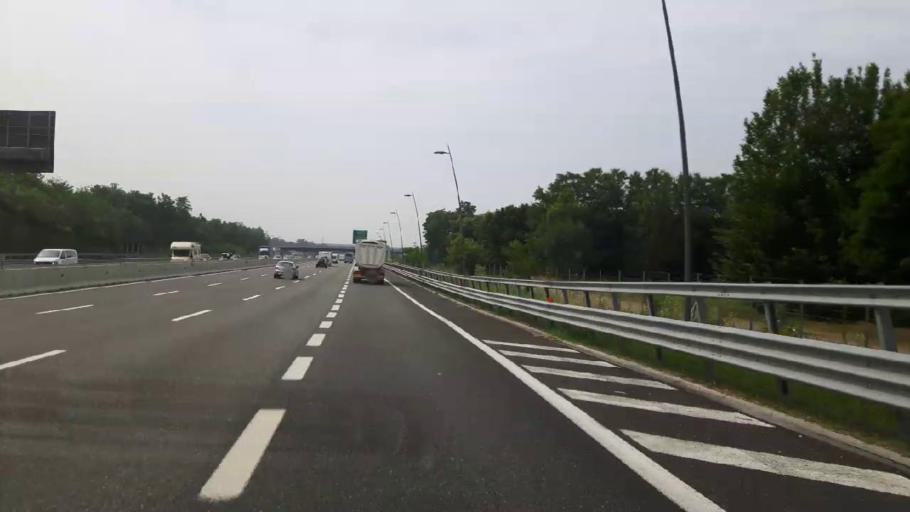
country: IT
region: Lombardy
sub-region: Provincia di Como
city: Cirimido
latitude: 45.6867
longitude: 9.0165
